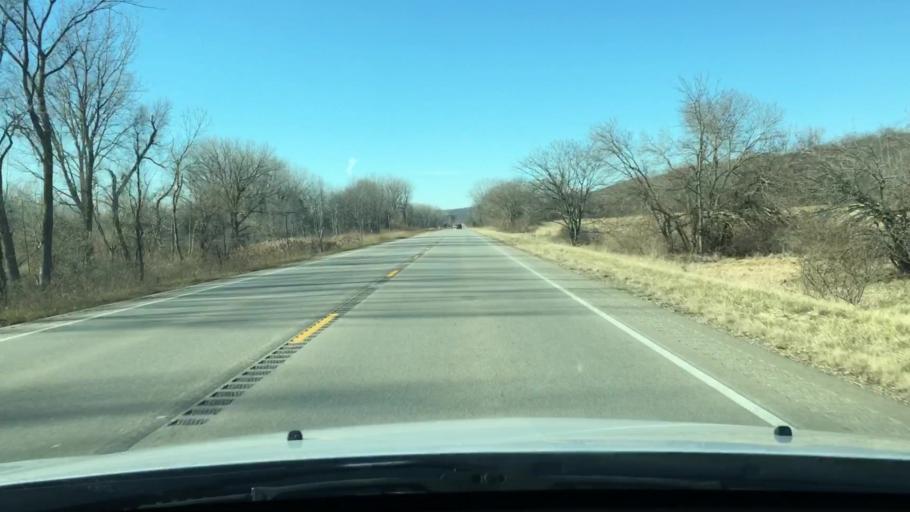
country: US
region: Illinois
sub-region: Peoria County
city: Glasford
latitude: 40.5508
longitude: -89.8172
